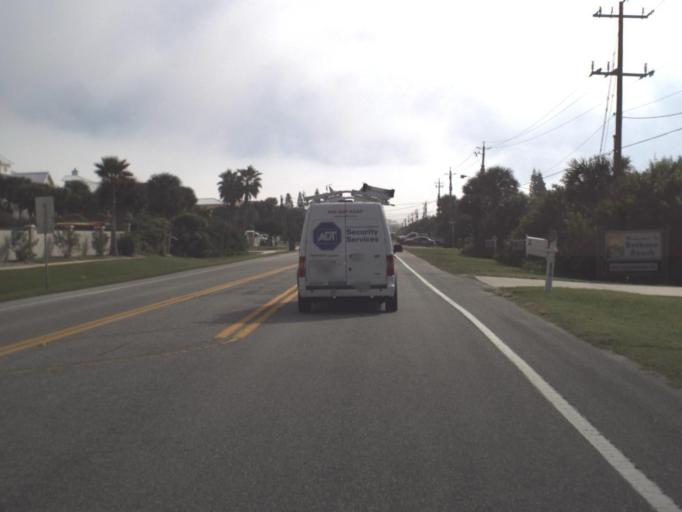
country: US
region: Florida
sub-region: Volusia County
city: Edgewater
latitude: 28.9700
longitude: -80.8532
